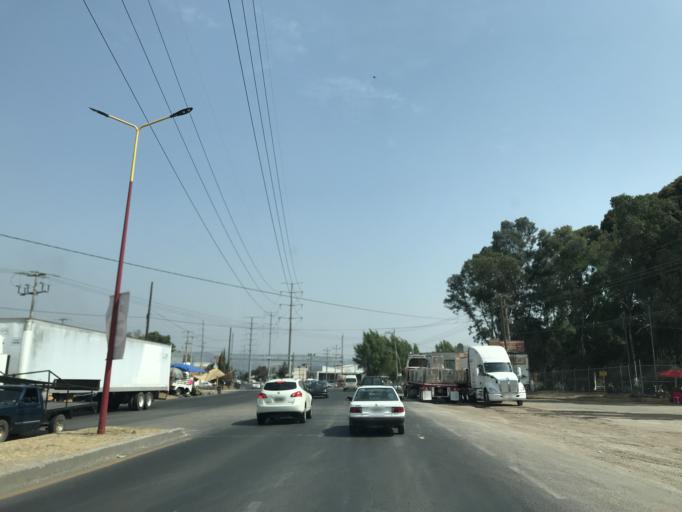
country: MX
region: Tlaxcala
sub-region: Chiautempan
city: Santa Cruz Tetela
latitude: 19.2971
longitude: -98.1953
